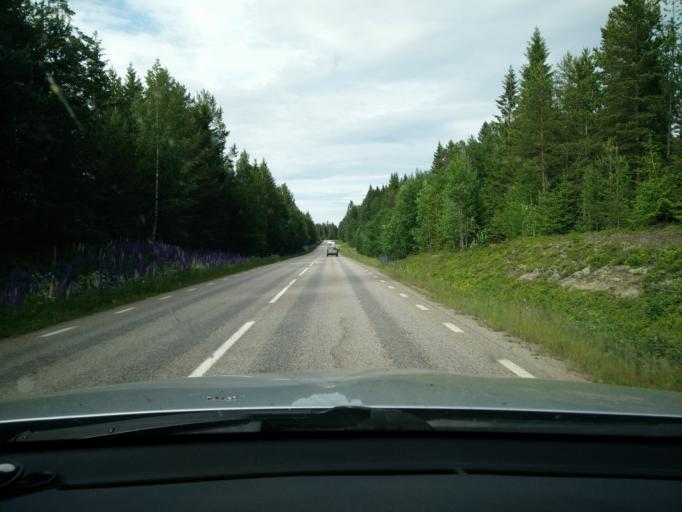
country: SE
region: Gaevleborg
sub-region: Nordanstigs Kommun
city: Bergsjoe
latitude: 61.9311
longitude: 17.0343
